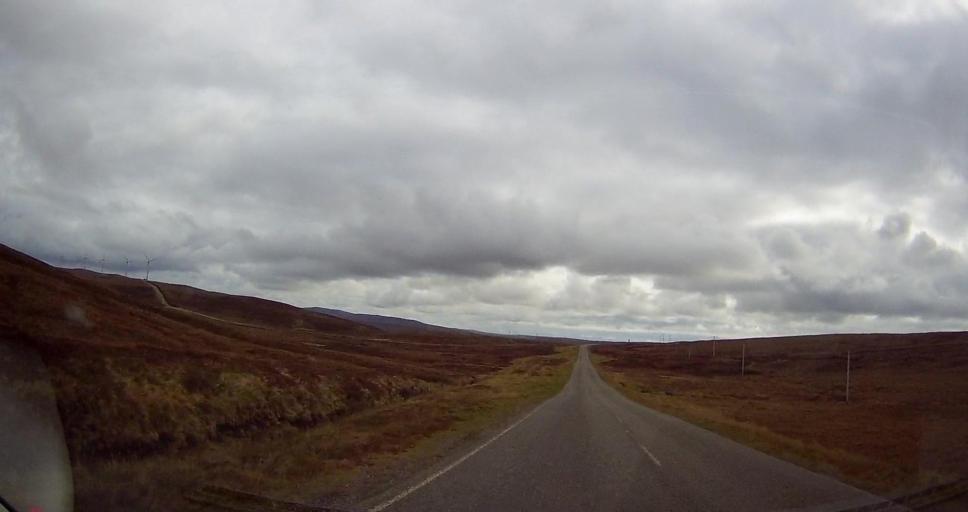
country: GB
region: Scotland
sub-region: Shetland Islands
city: Shetland
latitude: 60.6657
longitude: -1.0200
